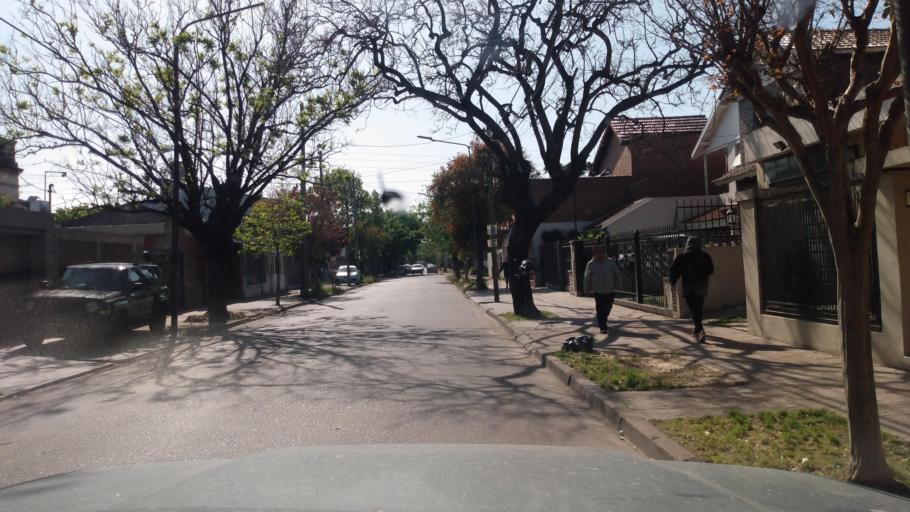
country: AR
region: Buenos Aires
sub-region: Partido de Moron
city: Moron
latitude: -34.6462
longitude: -58.5878
